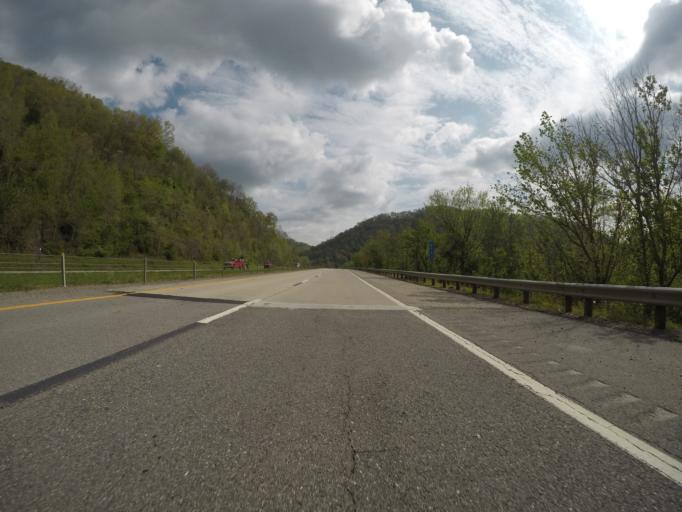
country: US
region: West Virginia
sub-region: Boone County
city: Madison
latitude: 38.1312
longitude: -81.8392
